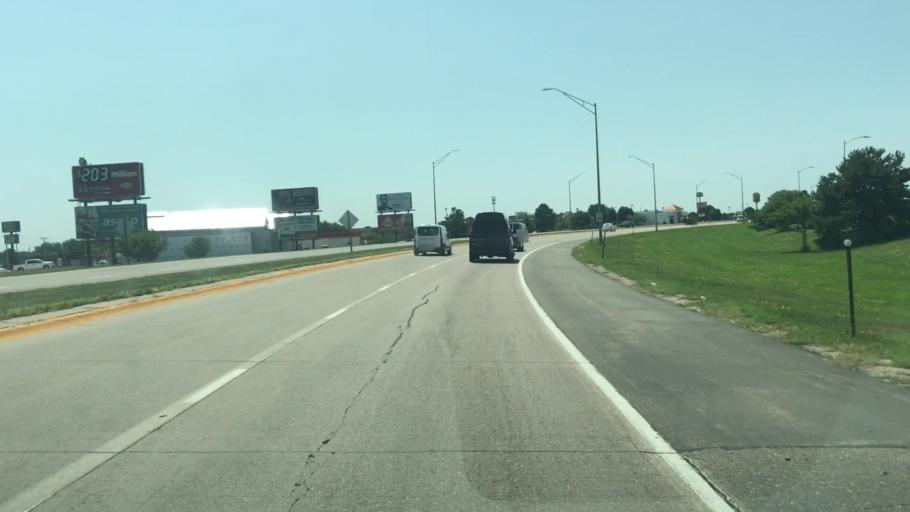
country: US
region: Nebraska
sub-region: Adams County
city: Hastings
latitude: 40.6120
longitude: -98.3834
